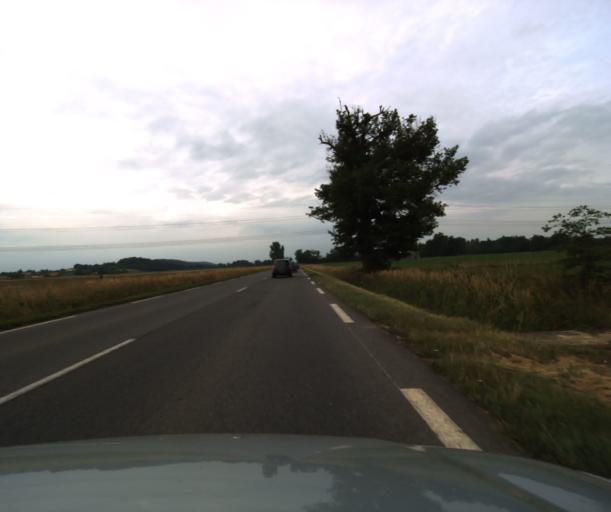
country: FR
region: Midi-Pyrenees
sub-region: Departement des Hautes-Pyrenees
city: Rabastens-de-Bigorre
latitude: 43.3710
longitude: 0.1445
